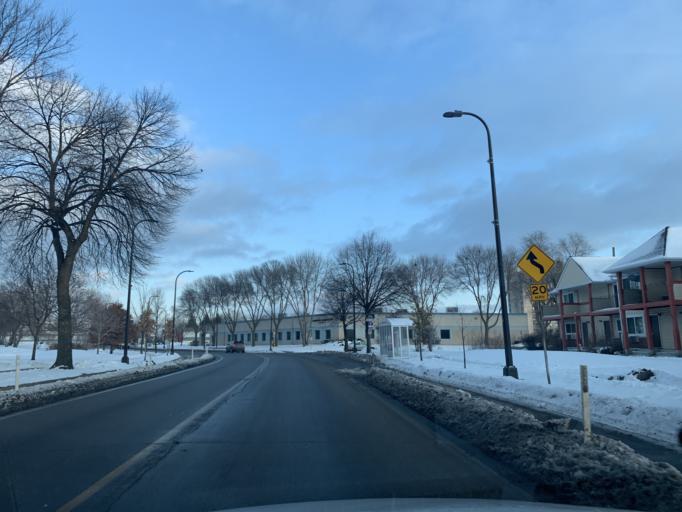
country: US
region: Minnesota
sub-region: Hennepin County
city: Minneapolis
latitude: 44.9915
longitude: -93.2992
